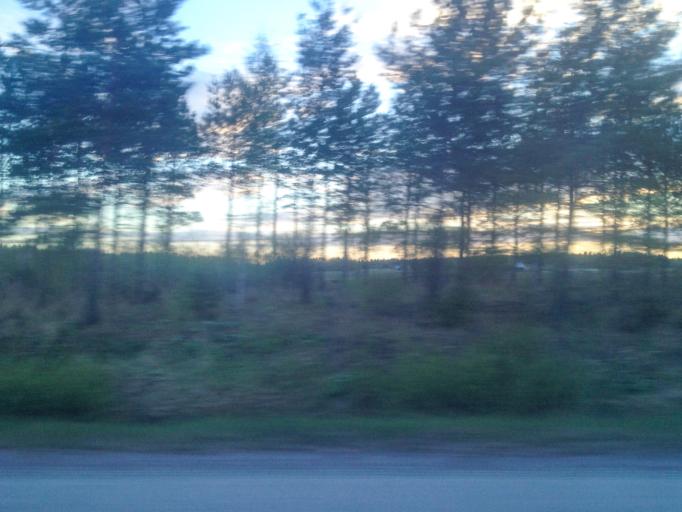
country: FI
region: Uusimaa
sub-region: Helsinki
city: Nurmijaervi
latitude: 60.5127
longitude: 24.8473
